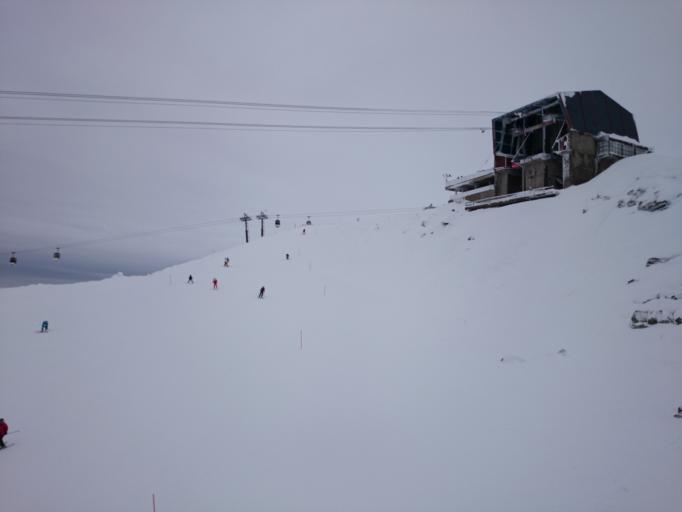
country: SE
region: Jaemtland
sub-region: Are Kommun
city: Are
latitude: 63.4263
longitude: 13.0808
